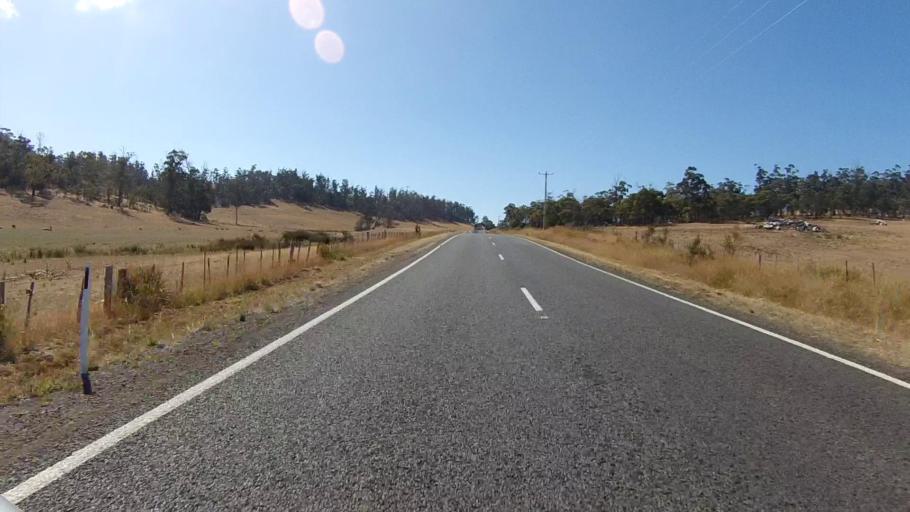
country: AU
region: Tasmania
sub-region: Sorell
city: Sorell
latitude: -42.4327
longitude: 147.9312
